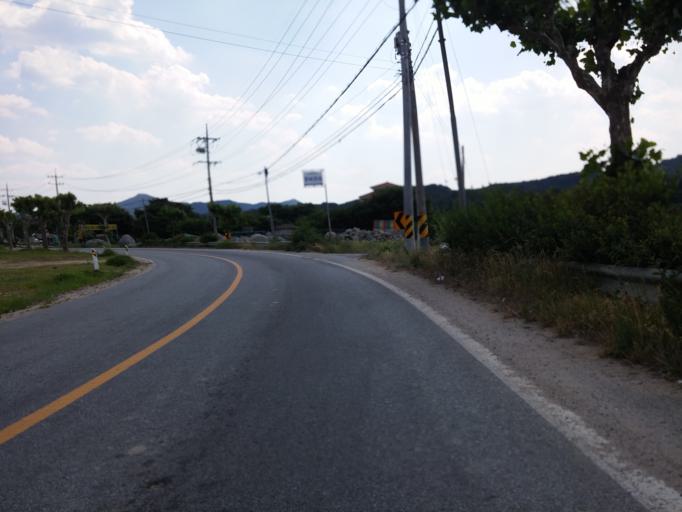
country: KR
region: Chungcheongbuk-do
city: Cheongju-si
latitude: 36.5639
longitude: 127.5075
